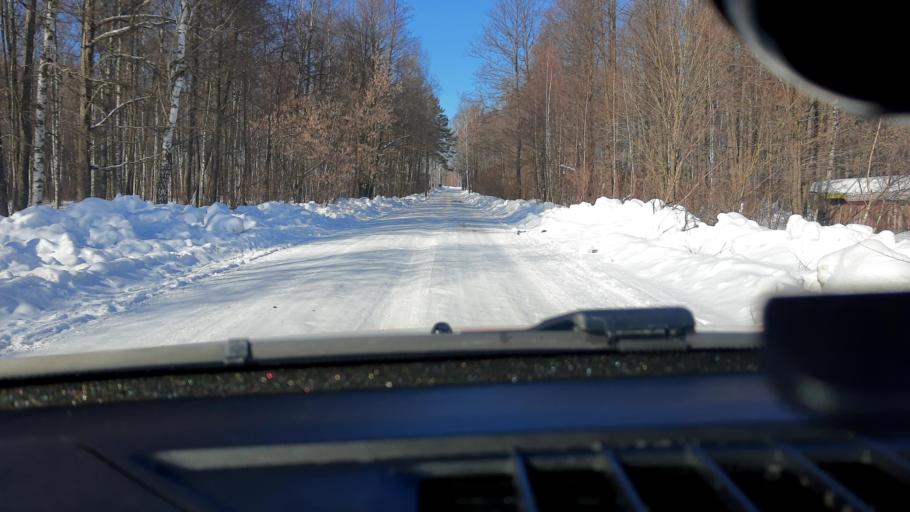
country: RU
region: Nizjnij Novgorod
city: Yuganets
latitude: 56.2493
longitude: 43.2245
